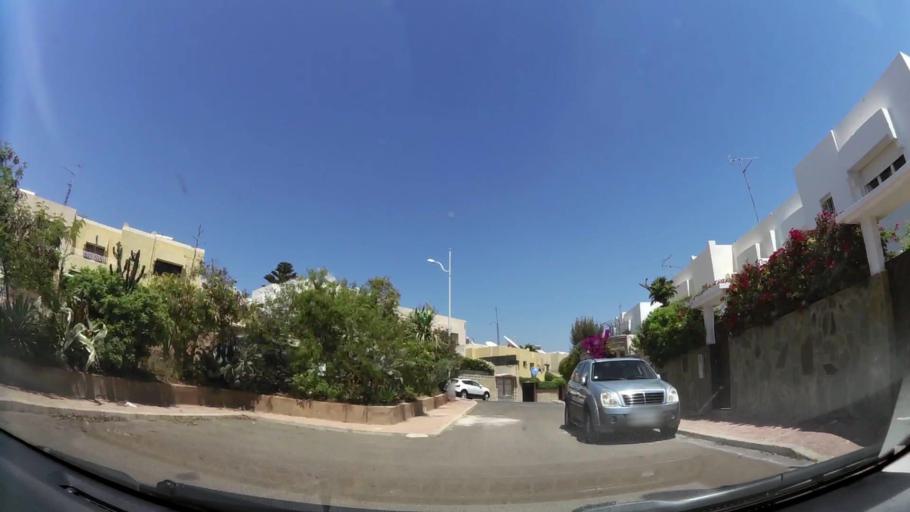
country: MA
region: Souss-Massa-Draa
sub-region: Agadir-Ida-ou-Tnan
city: Agadir
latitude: 30.4335
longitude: -9.5842
